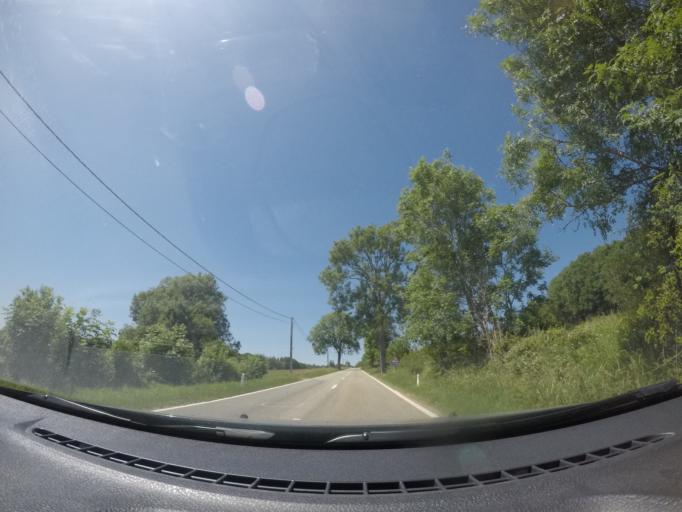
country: BE
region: Wallonia
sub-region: Province du Luxembourg
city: Daverdisse
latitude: 50.0201
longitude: 5.1658
